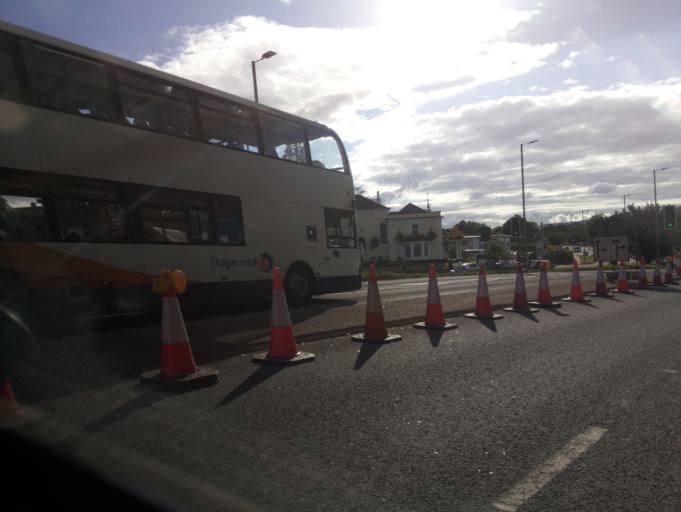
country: GB
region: England
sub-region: Devon
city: Exminster
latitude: 50.6925
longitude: -3.5165
